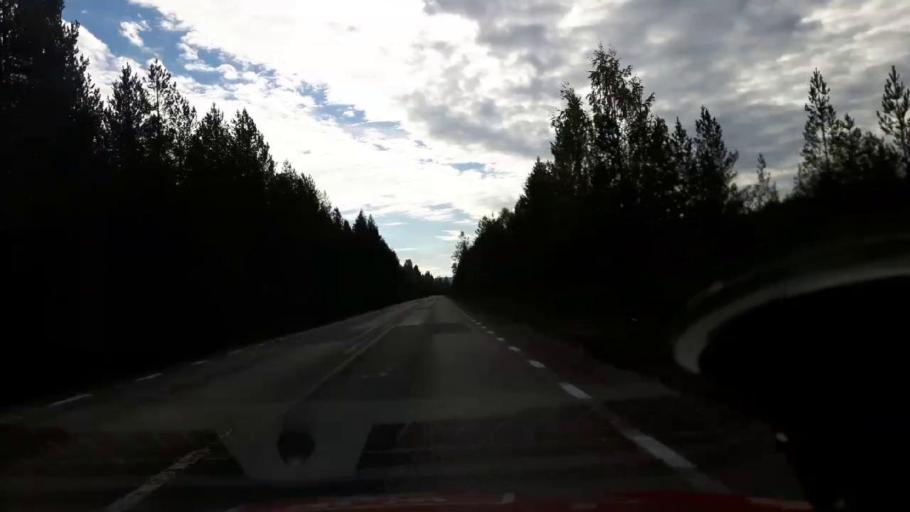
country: SE
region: Gaevleborg
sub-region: Ljusdals Kommun
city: Farila
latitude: 61.9709
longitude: 15.3468
